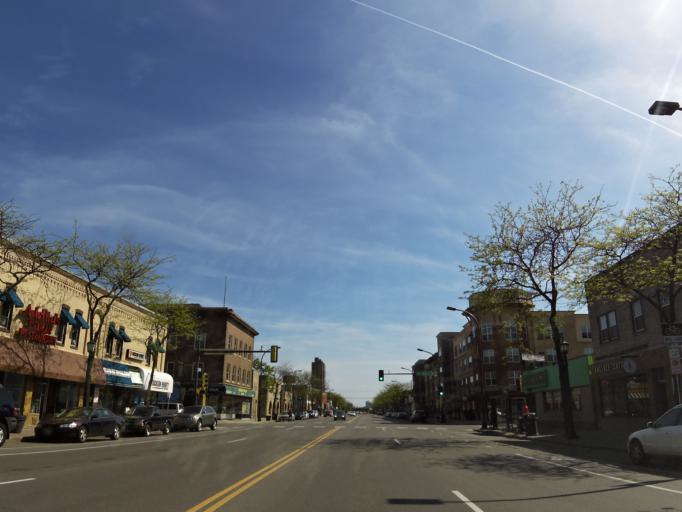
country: US
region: Minnesota
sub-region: Hennepin County
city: Saint Anthony
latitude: 45.0127
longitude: -93.2474
